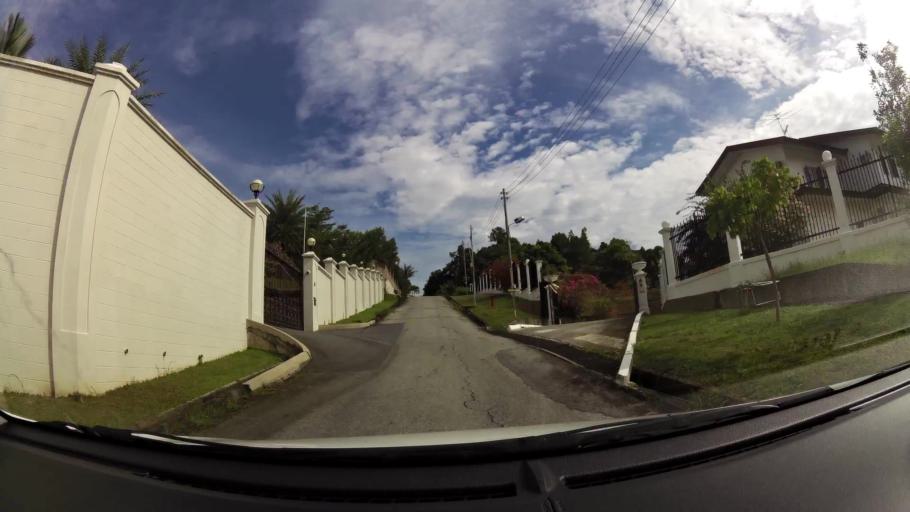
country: BN
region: Brunei and Muara
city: Bandar Seri Begawan
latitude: 4.8914
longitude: 114.8958
